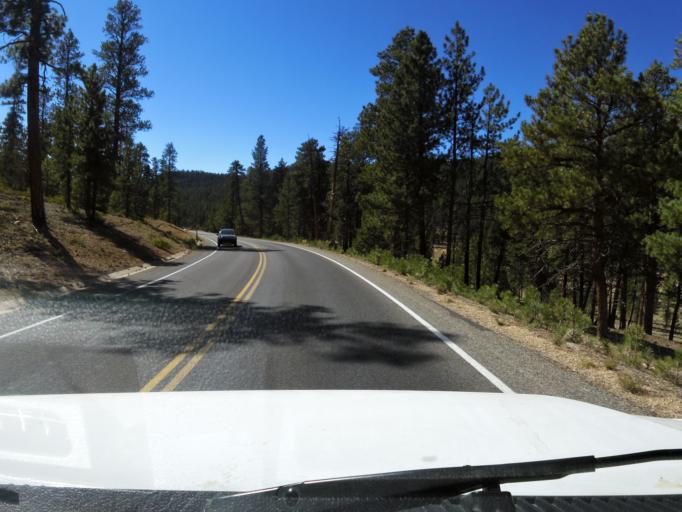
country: US
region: Utah
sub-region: Garfield County
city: Panguitch
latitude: 37.6054
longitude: -112.2053
